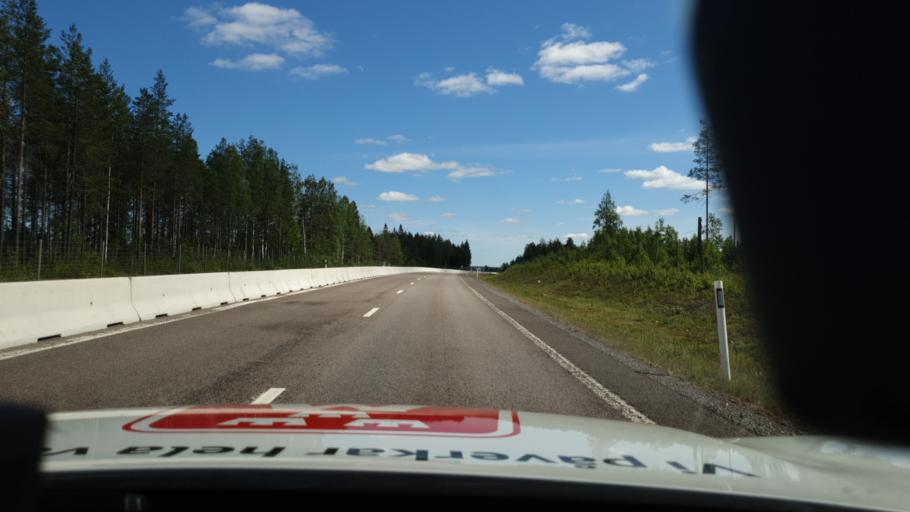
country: SE
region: Norrbotten
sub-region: Kalix Kommun
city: Toere
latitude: 65.9089
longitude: 22.8294
